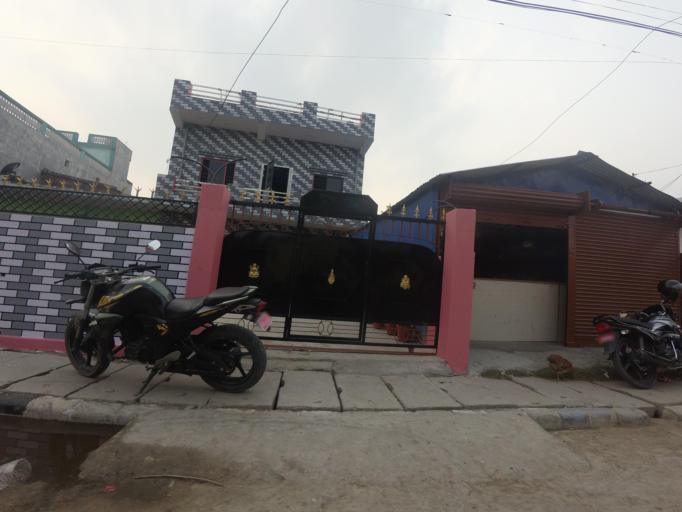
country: NP
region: Western Region
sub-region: Lumbini Zone
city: Bhairahawa
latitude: 27.5110
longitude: 83.4247
